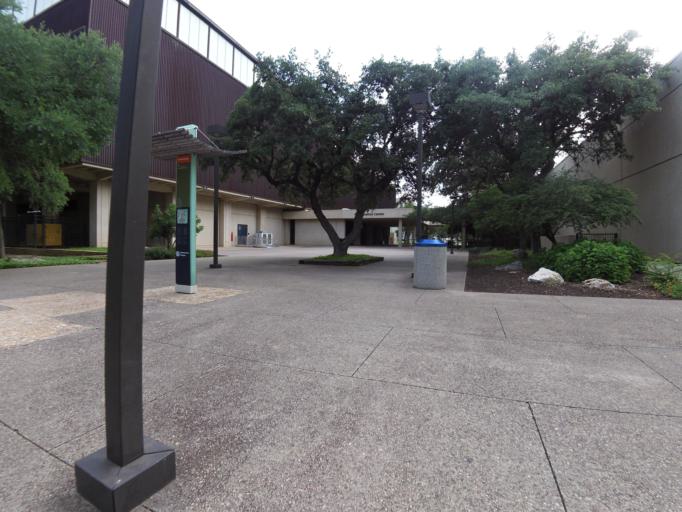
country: US
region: Texas
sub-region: Bexar County
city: Shavano Park
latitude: 29.5830
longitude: -98.6212
